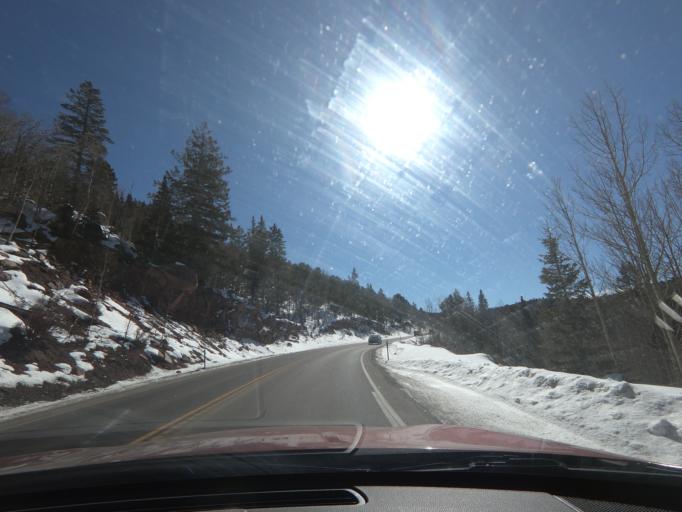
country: US
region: Colorado
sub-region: Teller County
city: Cripple Creek
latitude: 38.8097
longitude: -105.1252
